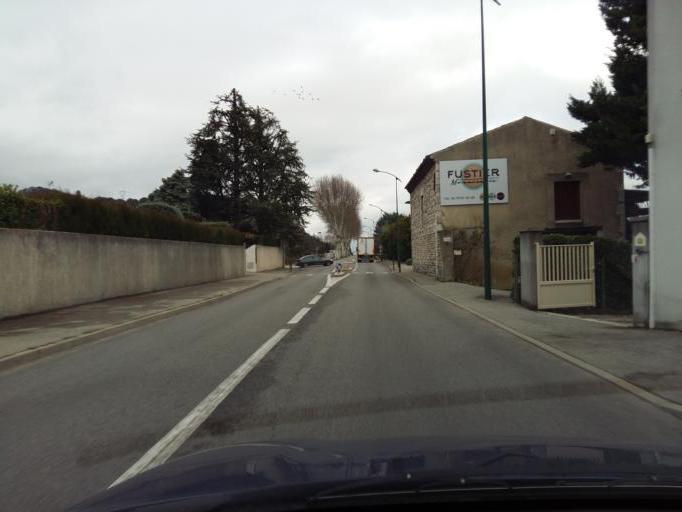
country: FR
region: Rhone-Alpes
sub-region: Departement de l'Ardeche
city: Cornas
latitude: 44.9647
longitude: 4.8492
